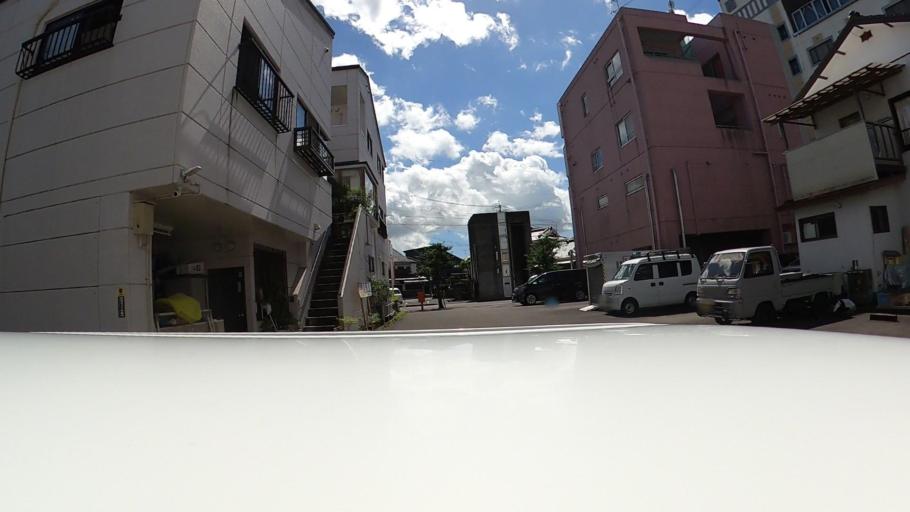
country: JP
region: Miyazaki
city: Tsuma
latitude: 32.1112
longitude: 131.4054
